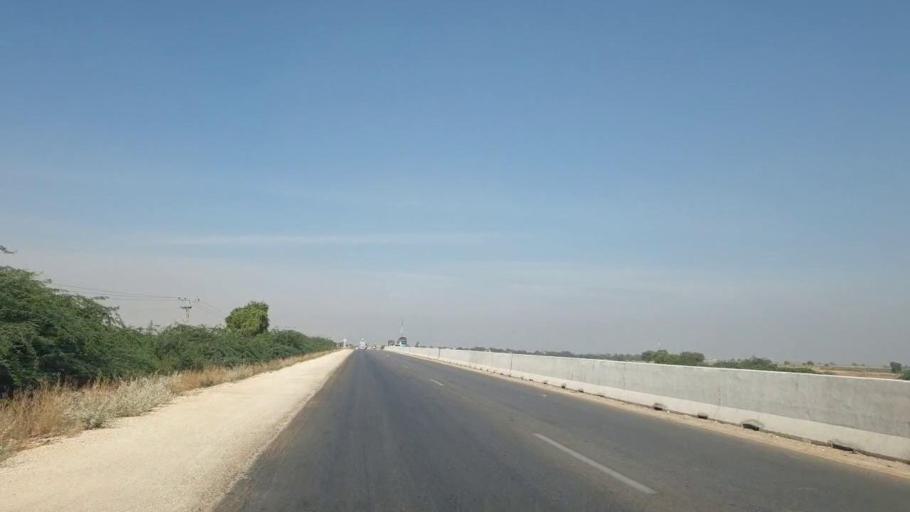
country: PK
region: Sindh
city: Matiari
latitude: 25.6402
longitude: 68.3014
